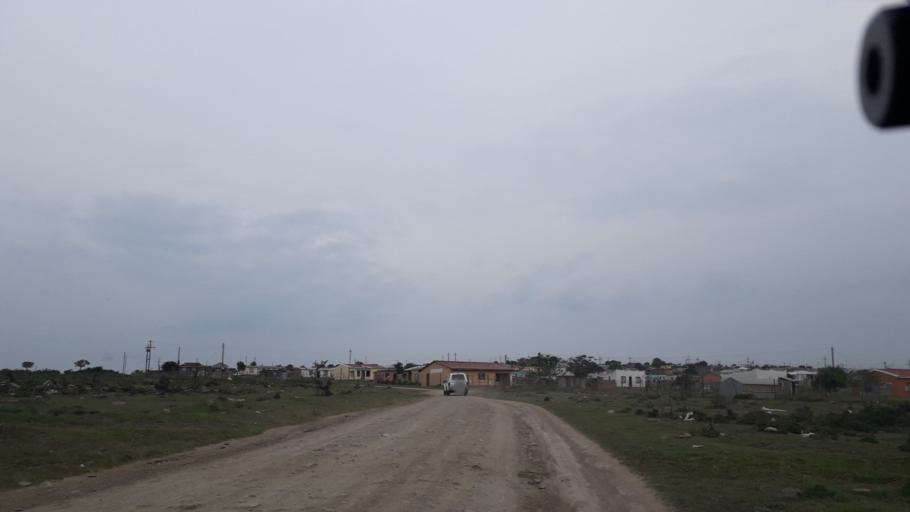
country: ZA
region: Eastern Cape
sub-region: Buffalo City Metropolitan Municipality
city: Bhisho
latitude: -32.8333
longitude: 27.3733
